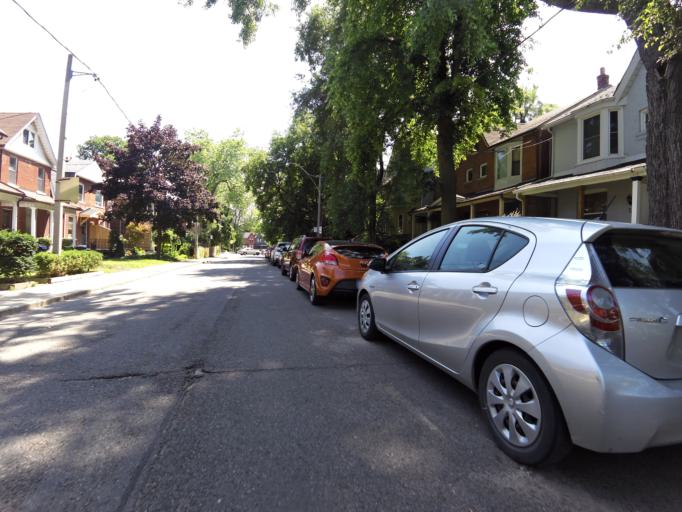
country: CA
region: Ontario
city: Toronto
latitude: 43.6680
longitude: -79.3476
